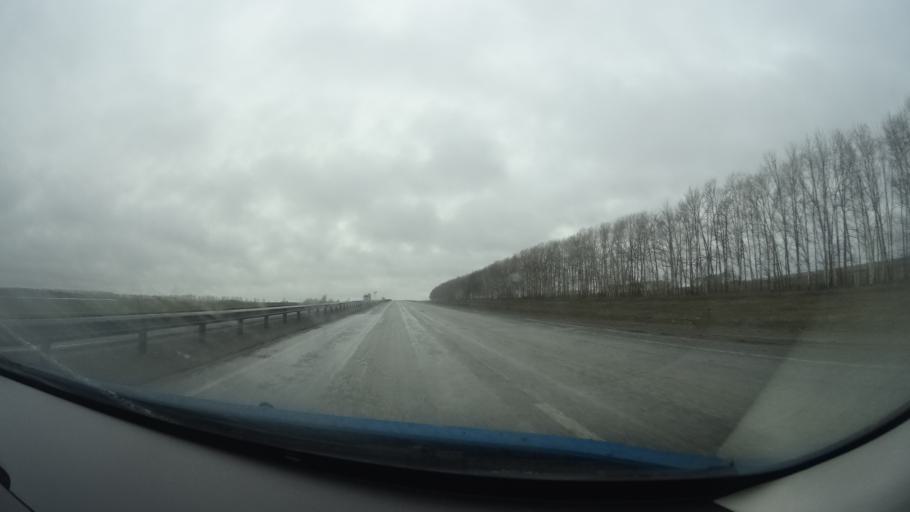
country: RU
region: Bashkortostan
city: Dmitriyevka
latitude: 54.7025
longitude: 55.2497
